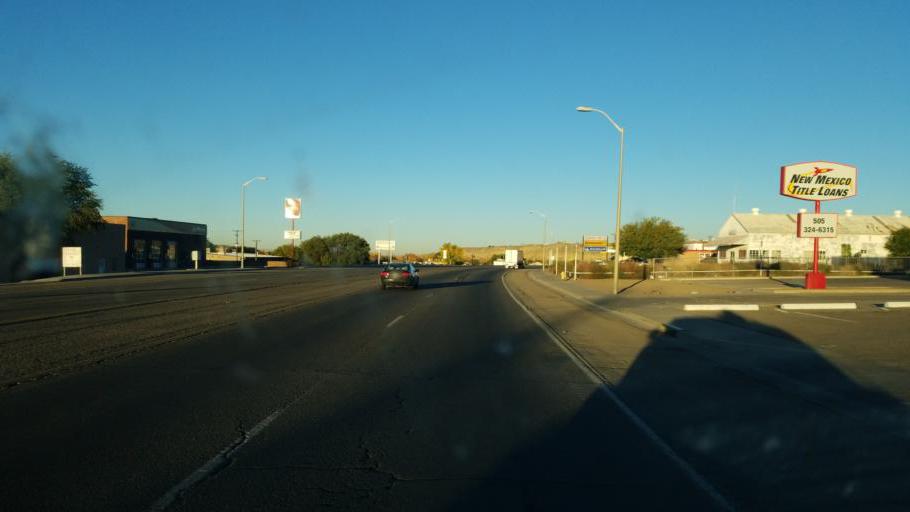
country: US
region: New Mexico
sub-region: San Juan County
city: Farmington
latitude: 36.7323
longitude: -108.2394
